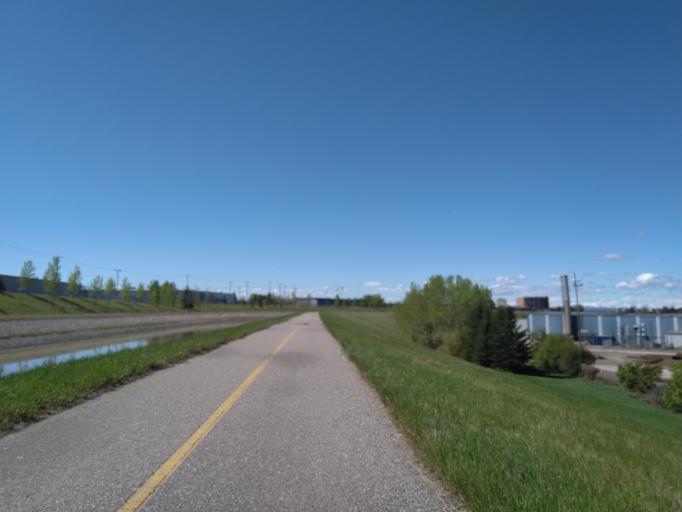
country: CA
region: Alberta
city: Calgary
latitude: 50.9863
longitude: -113.9887
